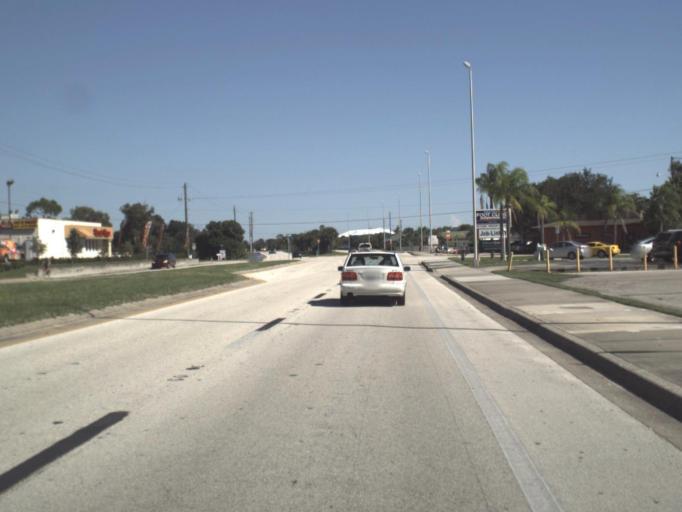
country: US
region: Florida
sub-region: Charlotte County
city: Manasota Key
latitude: 26.9374
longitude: -82.3347
